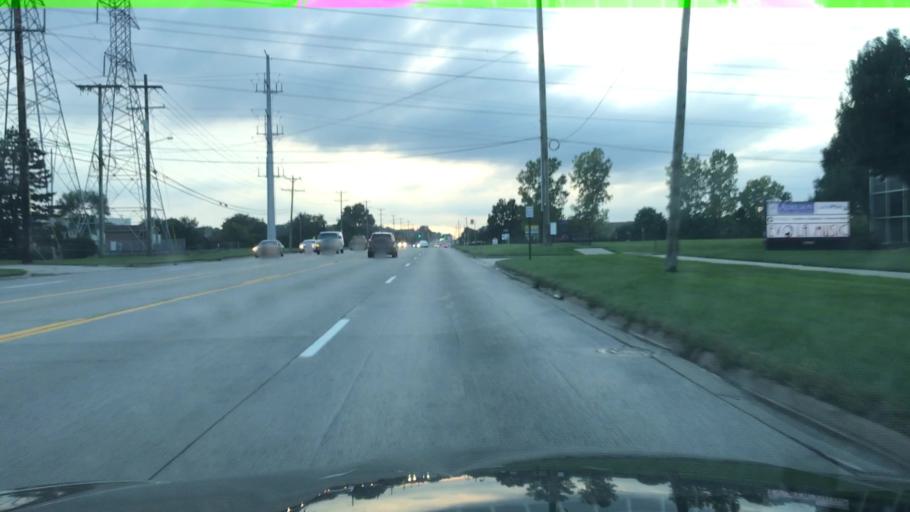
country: US
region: Michigan
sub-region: Macomb County
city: Shelby
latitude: 42.6700
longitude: -83.0026
